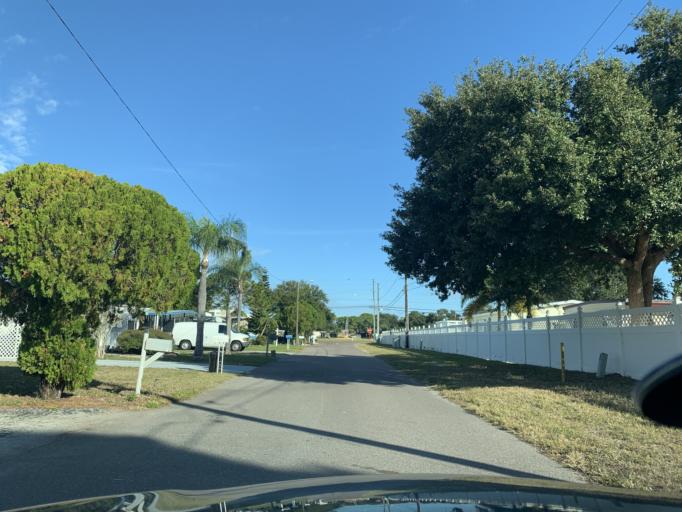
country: US
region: Florida
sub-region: Pinellas County
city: Kenneth City
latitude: 27.8199
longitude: -82.7477
